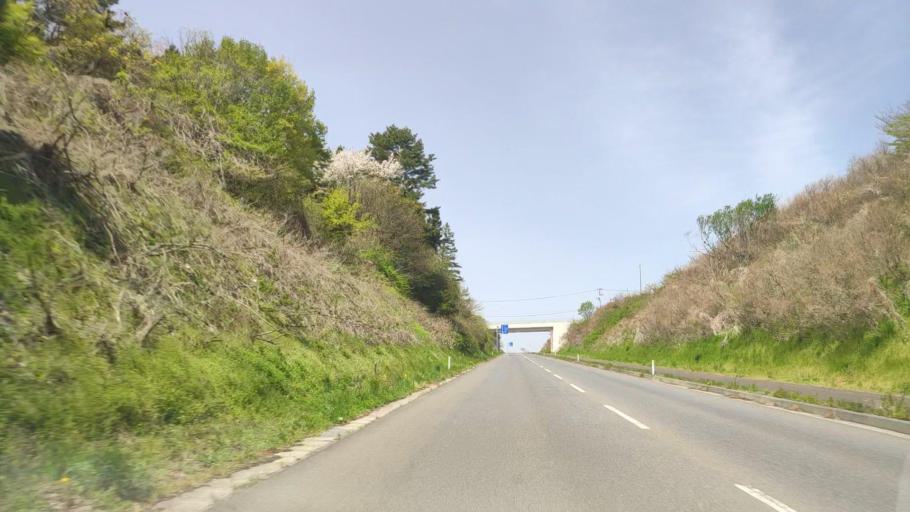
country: JP
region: Aomori
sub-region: Hachinohe Shi
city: Uchimaru
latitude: 40.5253
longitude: 141.4124
